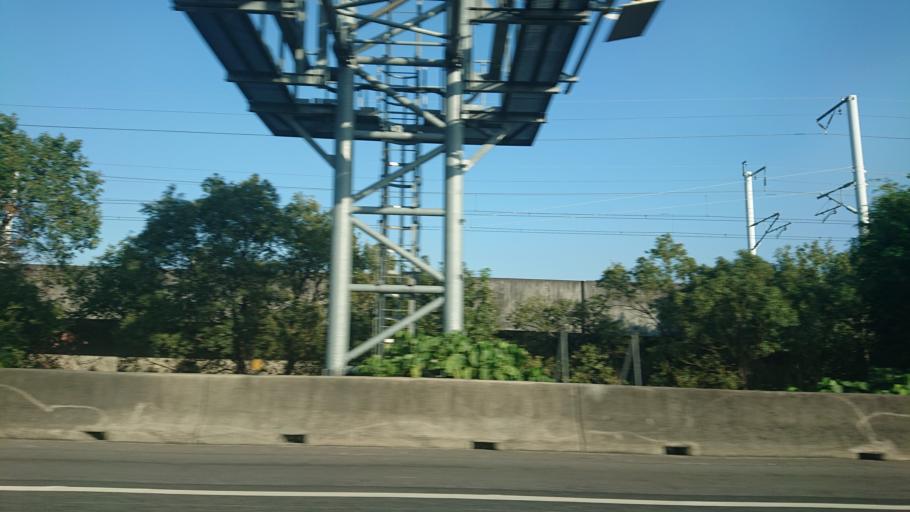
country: TW
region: Taiwan
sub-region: Taichung City
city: Taichung
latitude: 24.1307
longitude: 120.6174
